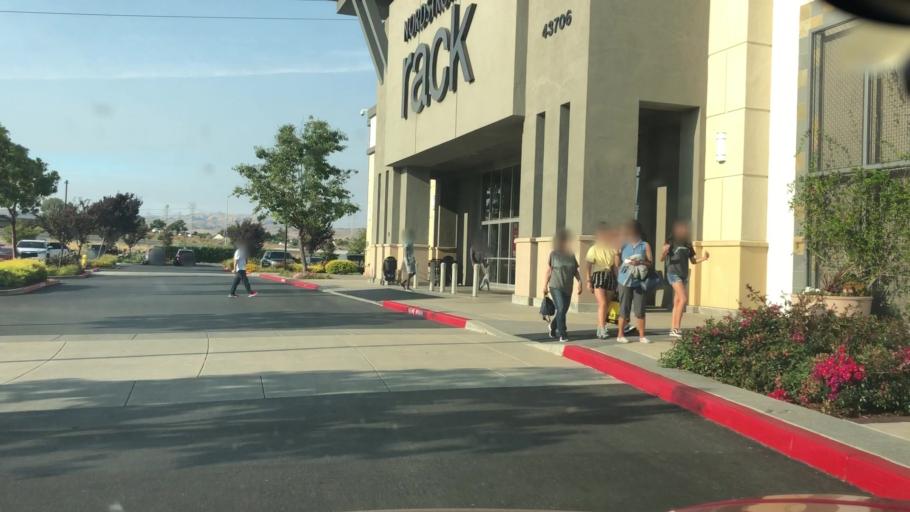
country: US
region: California
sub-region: Alameda County
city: Fremont
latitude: 37.5050
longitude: -121.9672
